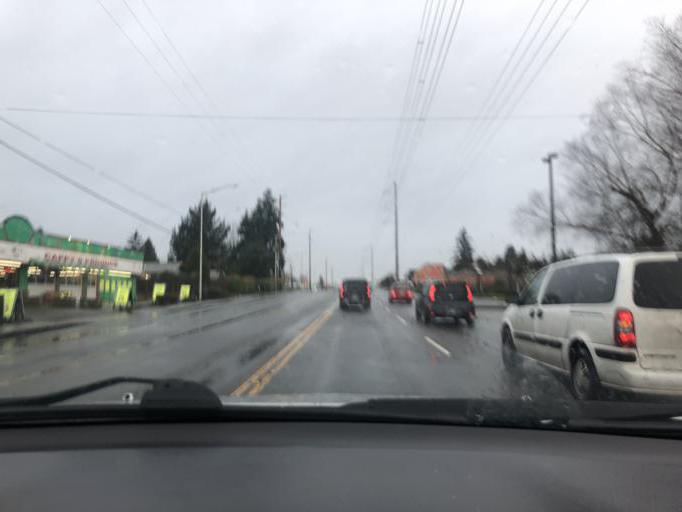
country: US
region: Washington
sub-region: Pierce County
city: Midland
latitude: 47.1918
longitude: -122.4109
